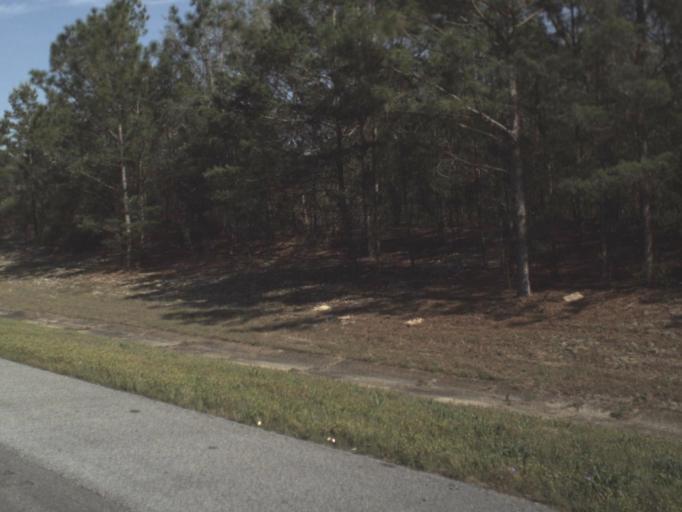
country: US
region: Florida
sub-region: Okaloosa County
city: Crestview
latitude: 30.7240
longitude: -86.4103
